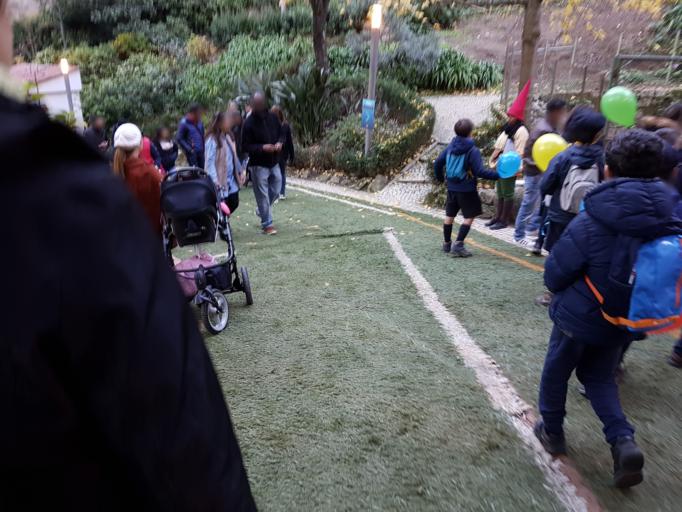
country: PT
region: Lisbon
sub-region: Sintra
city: Sintra
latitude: 38.7965
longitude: -9.3861
